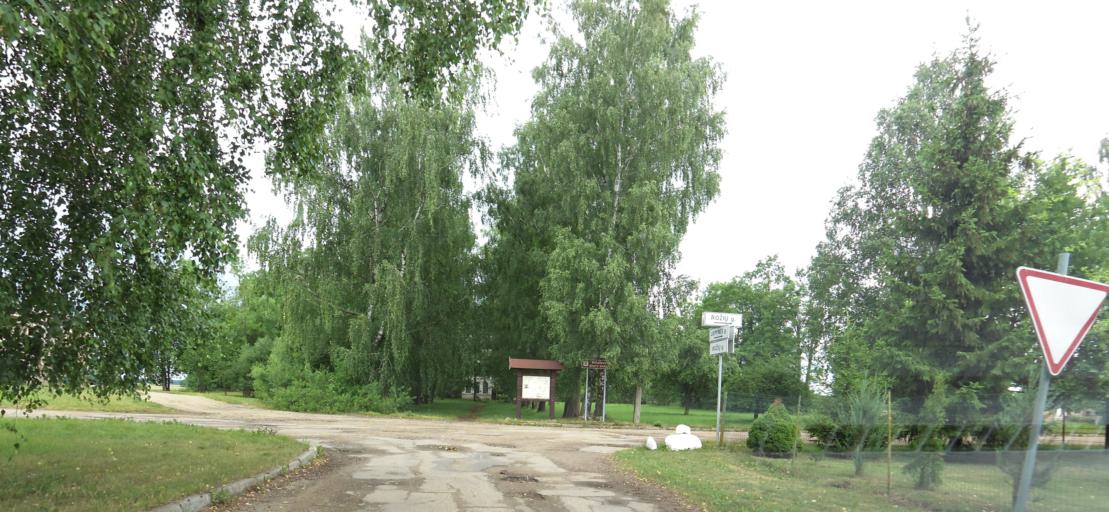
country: LT
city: Vabalninkas
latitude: 55.9075
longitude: 24.8067
